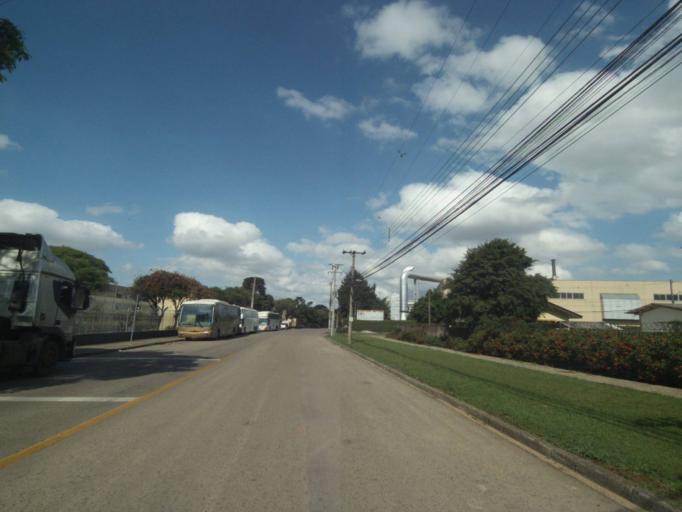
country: BR
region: Parana
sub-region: Curitiba
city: Curitiba
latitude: -25.4955
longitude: -49.3133
